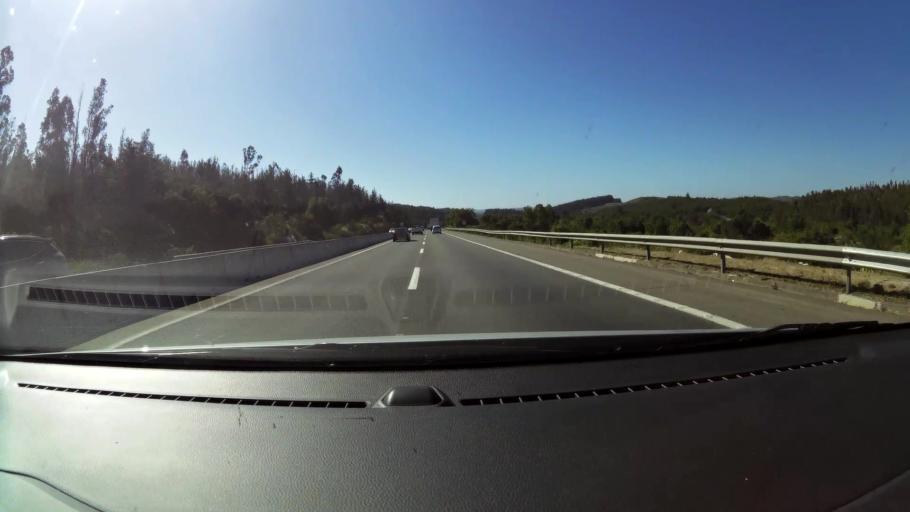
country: CL
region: Valparaiso
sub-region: Provincia de Marga Marga
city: Quilpue
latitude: -33.2025
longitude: -71.4872
